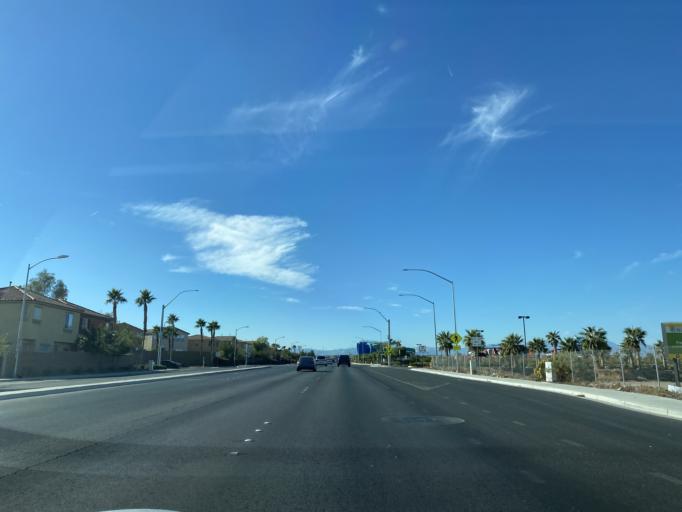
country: US
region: Nevada
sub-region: Clark County
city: Henderson
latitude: 36.0711
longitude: -115.0210
